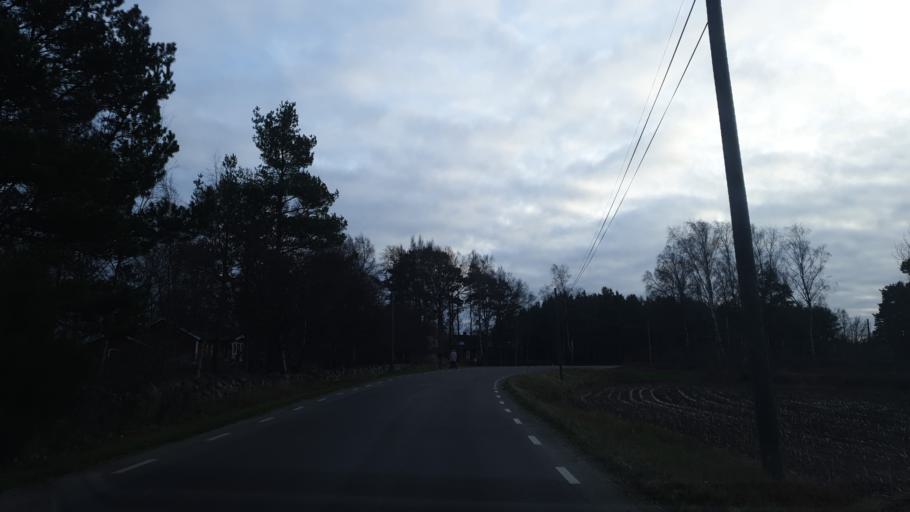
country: SE
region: Kalmar
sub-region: Torsas Kommun
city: Torsas
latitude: 56.2461
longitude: 16.0049
